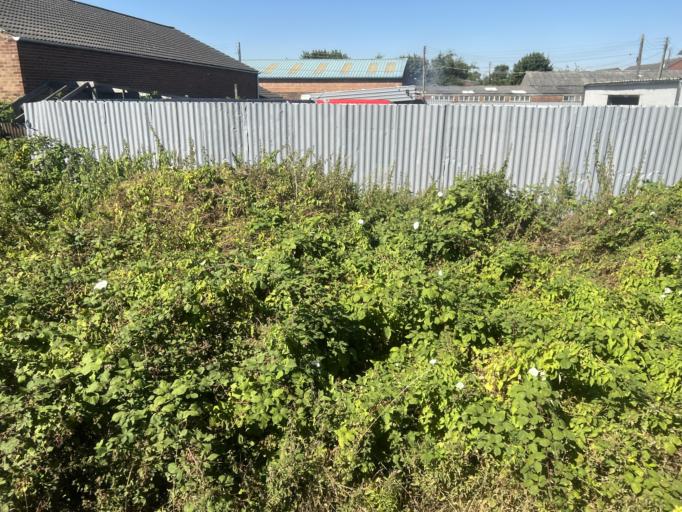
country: GB
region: England
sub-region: Lincolnshire
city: Boston
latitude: 52.9720
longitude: -0.0308
